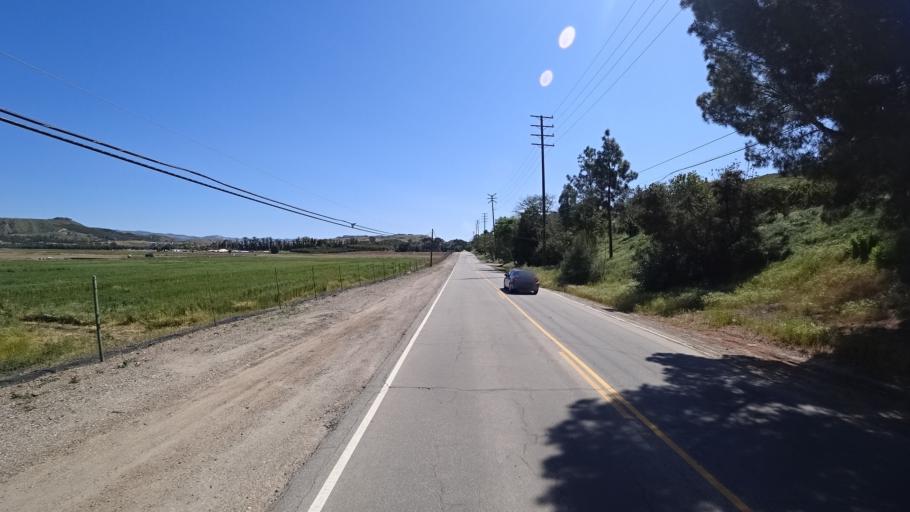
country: US
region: California
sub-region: Ventura County
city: Moorpark
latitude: 34.2499
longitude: -118.8591
